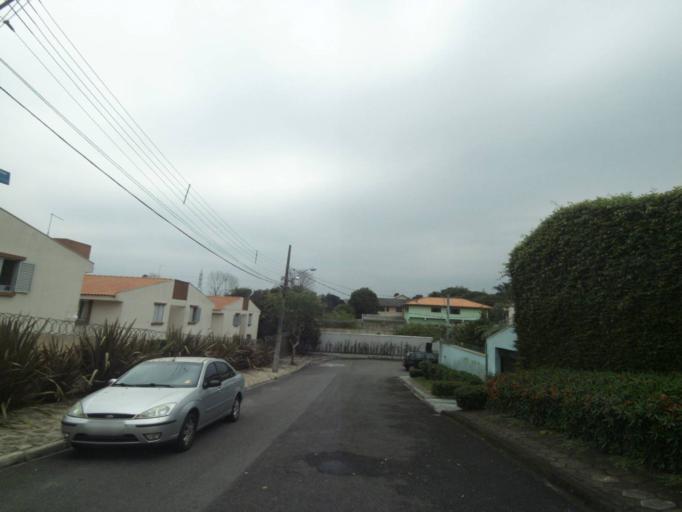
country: BR
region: Parana
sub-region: Curitiba
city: Curitiba
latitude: -25.4721
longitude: -49.3151
